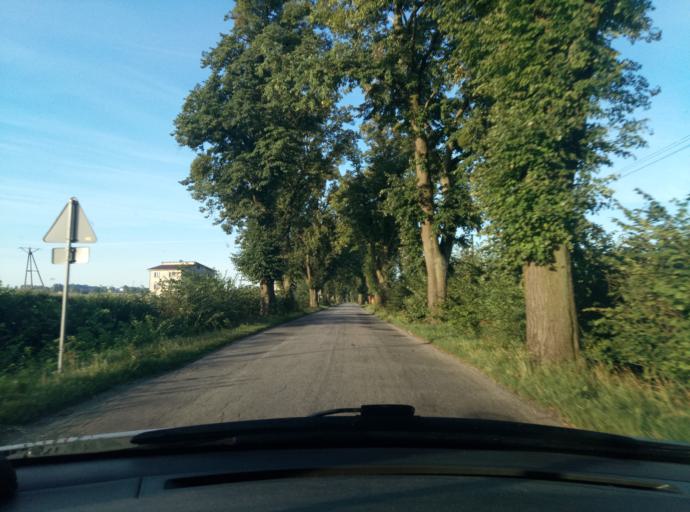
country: PL
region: Kujawsko-Pomorskie
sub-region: Powiat brodnicki
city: Jablonowo Pomorskie
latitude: 53.4054
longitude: 19.1713
